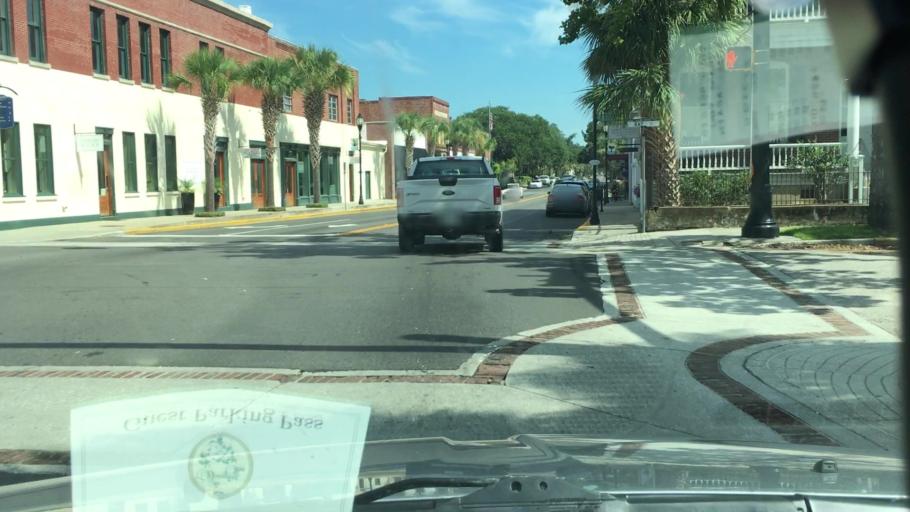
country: US
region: South Carolina
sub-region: Beaufort County
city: Beaufort
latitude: 32.4306
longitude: -80.6699
